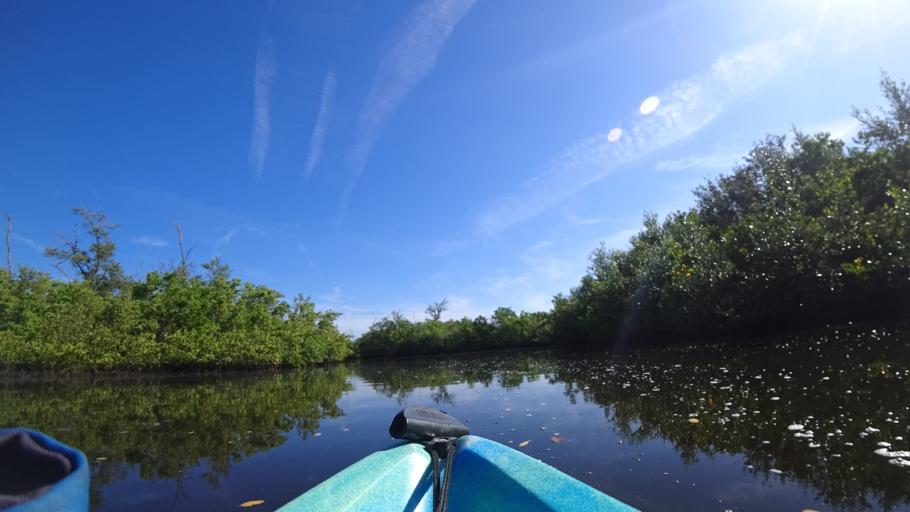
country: US
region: Florida
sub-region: Manatee County
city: Holmes Beach
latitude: 27.5099
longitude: -82.6717
